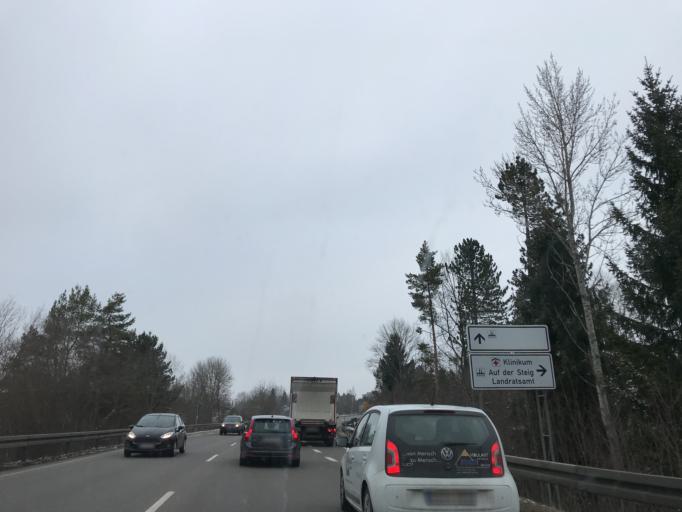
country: DE
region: Baden-Wuerttemberg
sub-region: Freiburg Region
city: Villingen-Schwenningen
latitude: 48.0567
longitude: 8.4711
